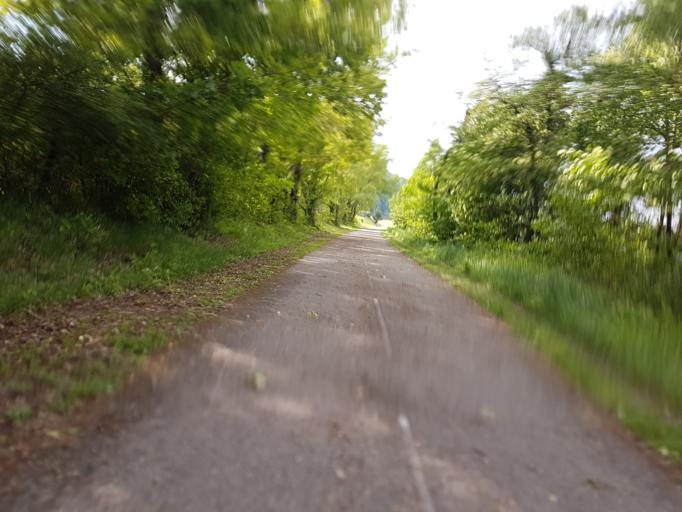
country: FR
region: Rhone-Alpes
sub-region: Departement de la Haute-Savoie
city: Versonnex
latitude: 45.9510
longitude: 5.8367
